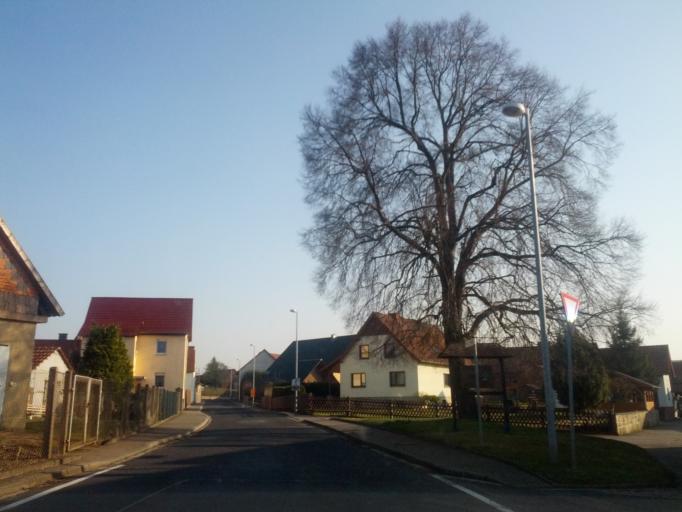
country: DE
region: Thuringia
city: Bischofroda
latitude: 51.0465
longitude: 10.3831
